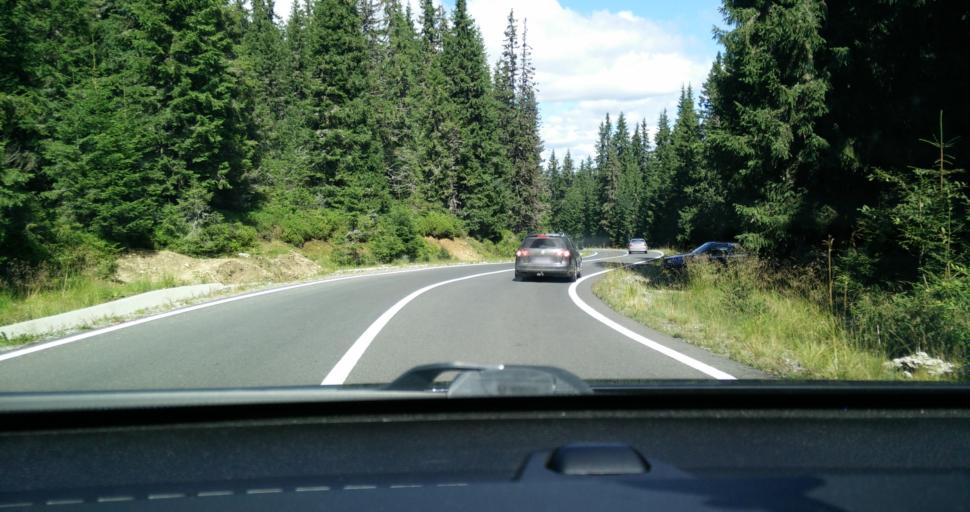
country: RO
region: Hunedoara
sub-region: Oras Petrila
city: Petrila
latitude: 45.4779
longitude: 23.6399
